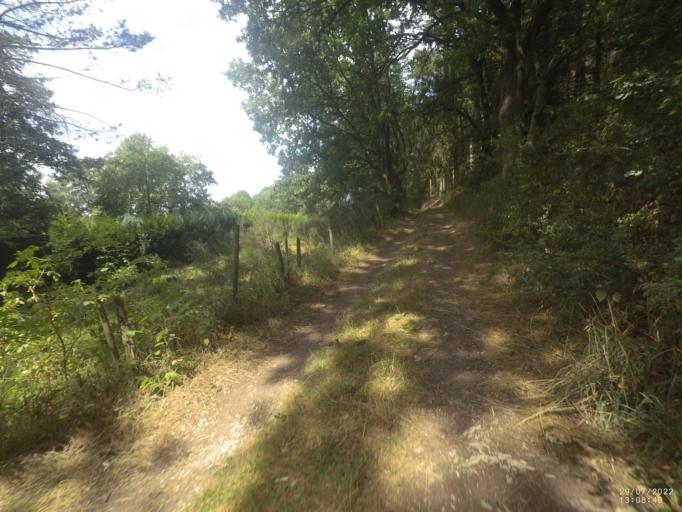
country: DE
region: Rheinland-Pfalz
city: Duppach
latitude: 50.2693
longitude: 6.5810
